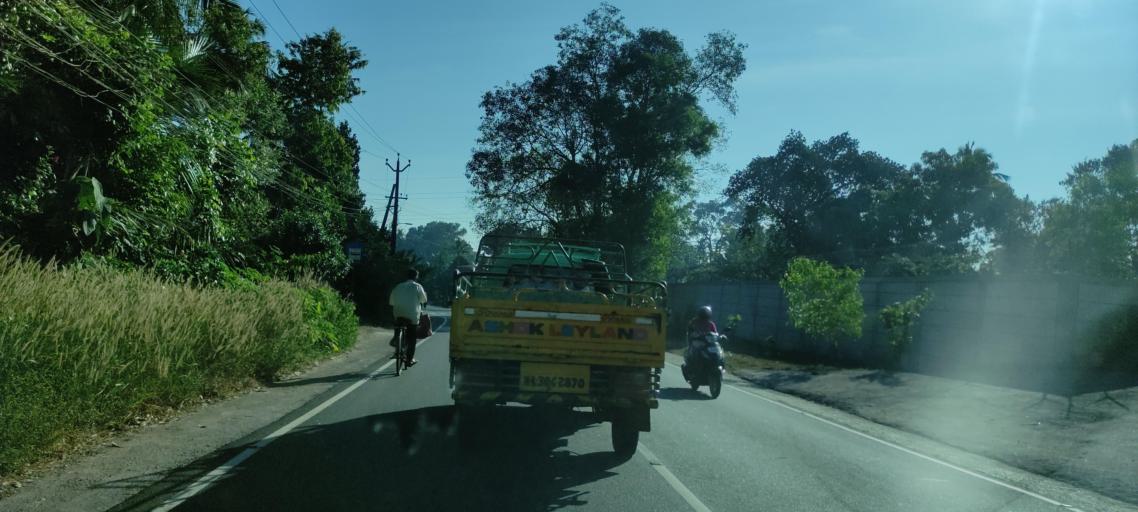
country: IN
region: Kerala
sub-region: Alappuzha
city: Kattanam
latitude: 9.1746
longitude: 76.6290
